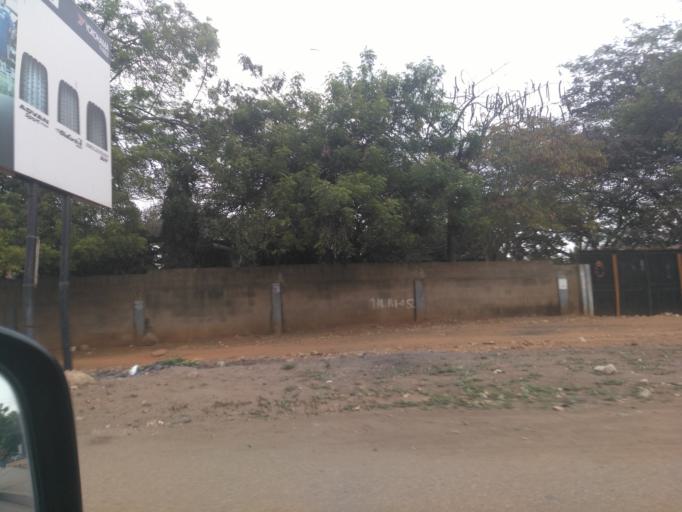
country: GH
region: Greater Accra
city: Accra
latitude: 5.5990
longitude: -0.1943
